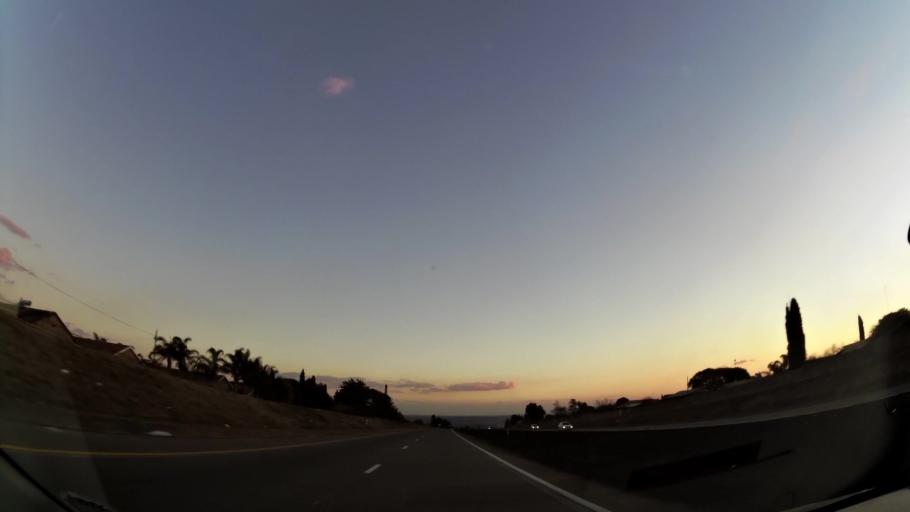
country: ZA
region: Mpumalanga
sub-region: Nkangala District Municipality
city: Witbank
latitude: -25.9078
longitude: 29.2455
